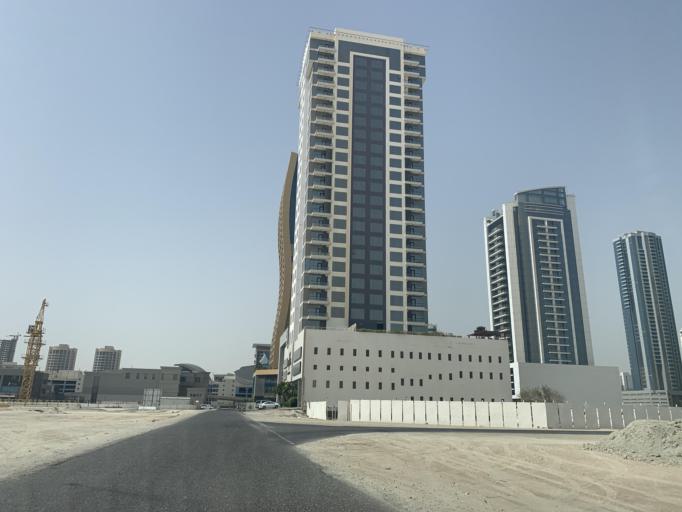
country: BH
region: Manama
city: Jidd Hafs
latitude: 26.2382
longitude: 50.5533
